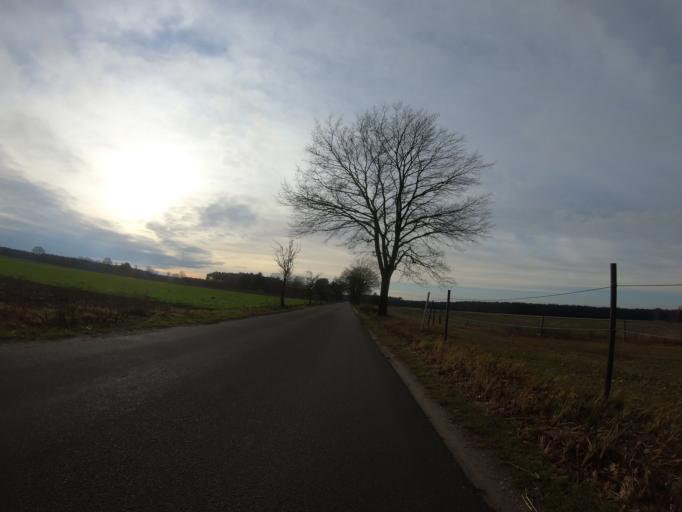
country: DE
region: Lower Saxony
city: Muden
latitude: 52.4976
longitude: 10.4065
